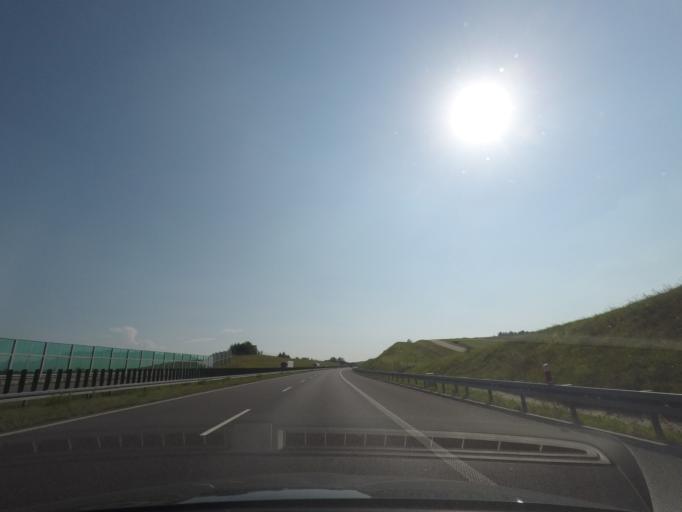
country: PL
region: Silesian Voivodeship
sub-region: Powiat wodzislawski
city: Polomia
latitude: 49.9821
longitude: 18.5582
